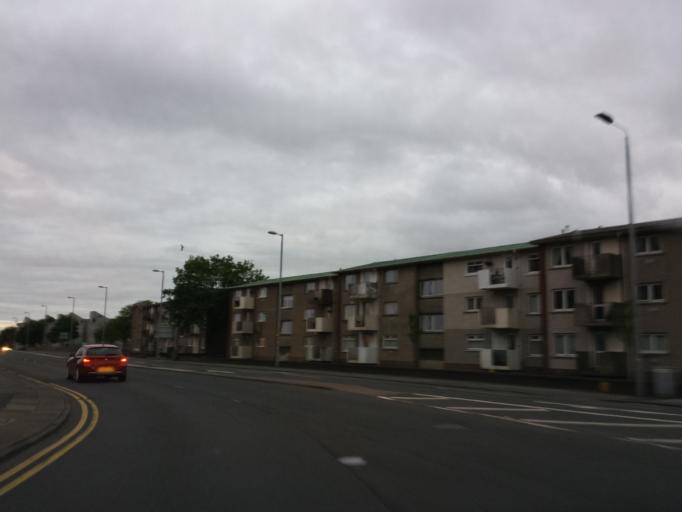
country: GB
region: Scotland
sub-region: South Ayrshire
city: Ayr
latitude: 55.4670
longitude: -4.6276
